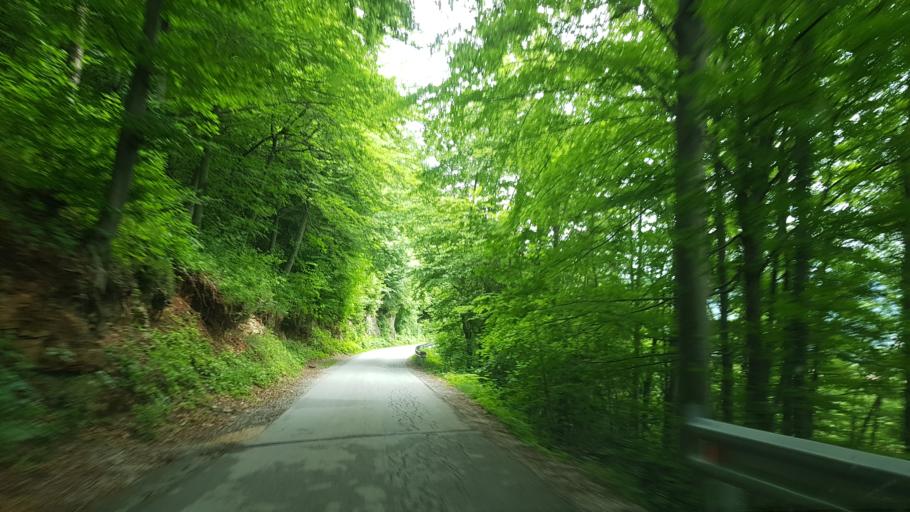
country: SI
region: Dobrna
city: Dobrna
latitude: 46.3524
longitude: 15.2374
